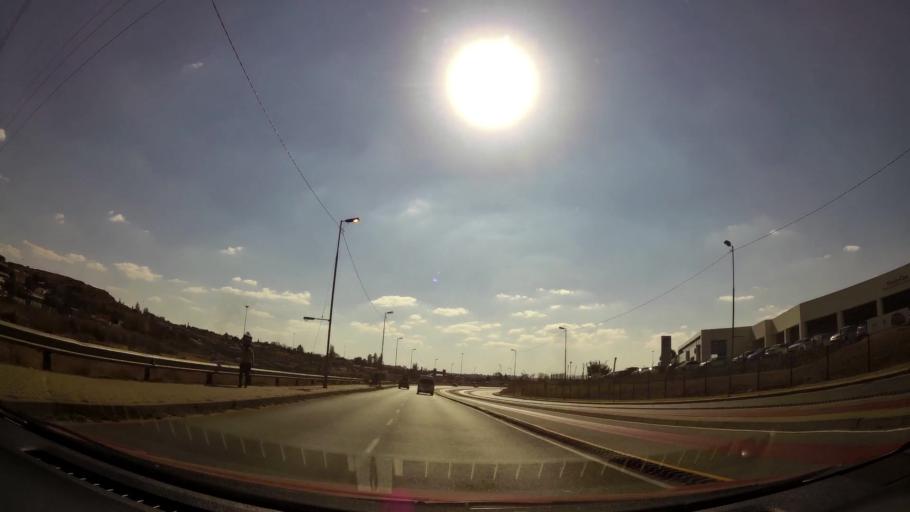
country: ZA
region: Gauteng
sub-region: City of Johannesburg Metropolitan Municipality
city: Soweto
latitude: -26.2439
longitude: 27.9106
